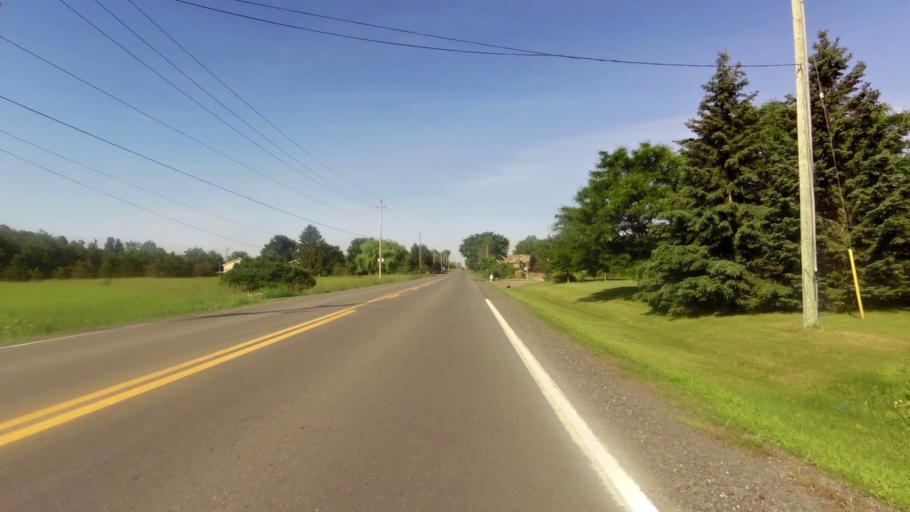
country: CA
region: Ontario
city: Ottawa
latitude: 45.2216
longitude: -75.5619
